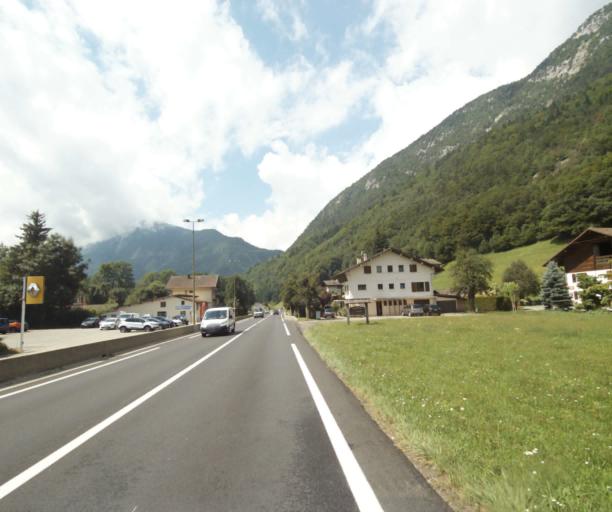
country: FR
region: Rhone-Alpes
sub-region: Departement de la Haute-Savoie
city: Thones
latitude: 45.8928
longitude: 6.3356
